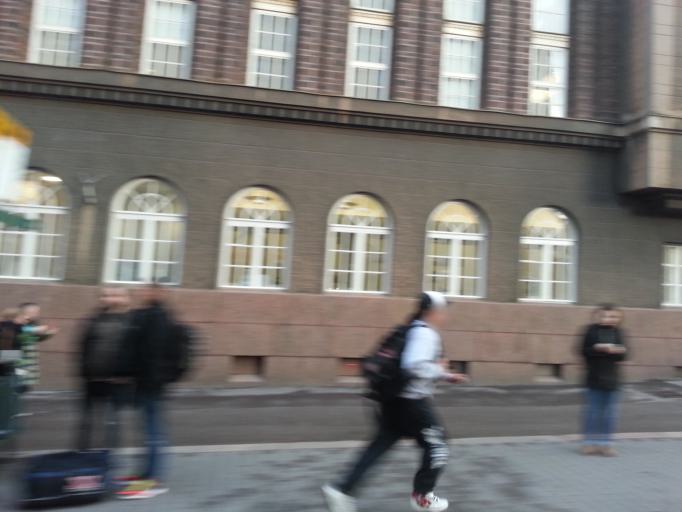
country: FI
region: Uusimaa
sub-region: Helsinki
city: Helsinki
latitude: 60.1860
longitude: 24.9514
